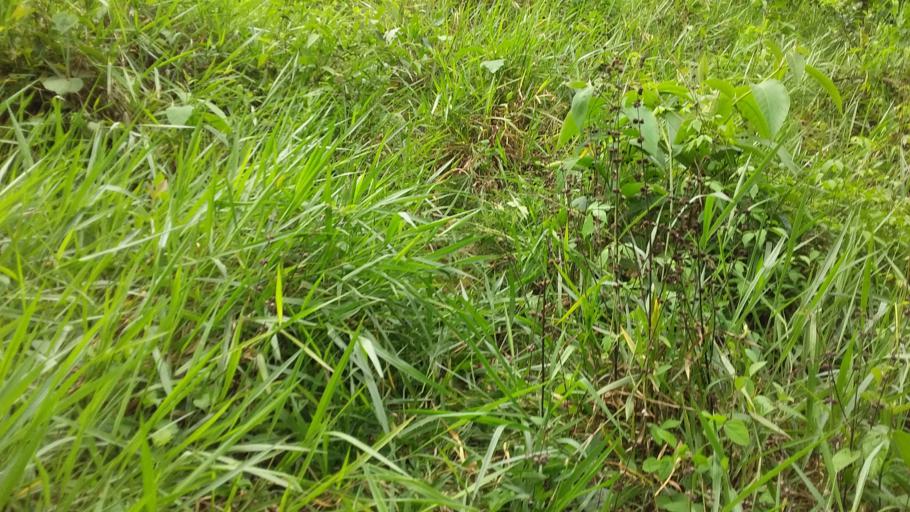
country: CO
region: Casanare
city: Nunchia
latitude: 5.6106
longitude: -72.2940
